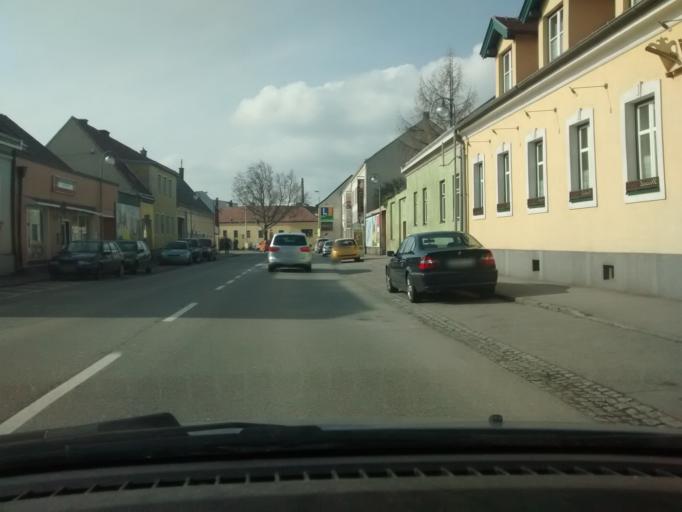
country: AT
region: Lower Austria
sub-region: Politischer Bezirk Baden
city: Traiskirchen
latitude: 48.0159
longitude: 16.2933
